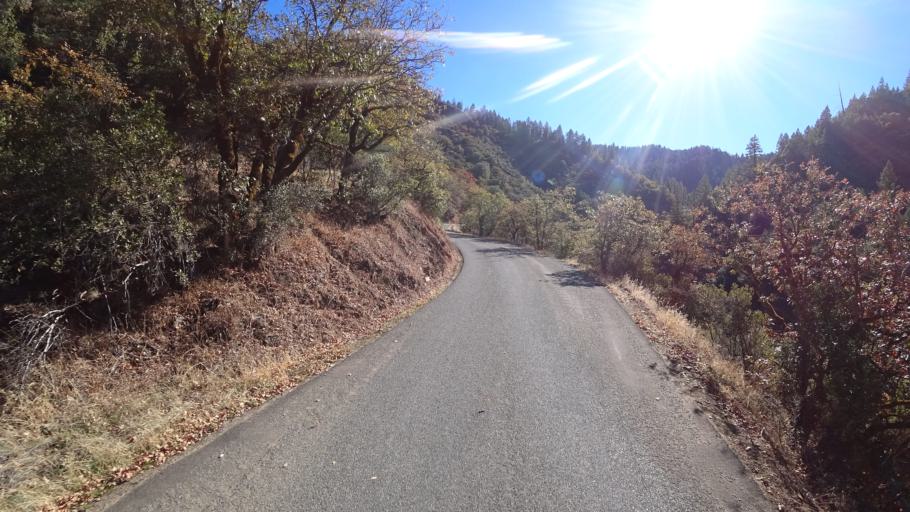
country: US
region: California
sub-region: Humboldt County
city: Willow Creek
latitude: 41.1648
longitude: -123.2112
